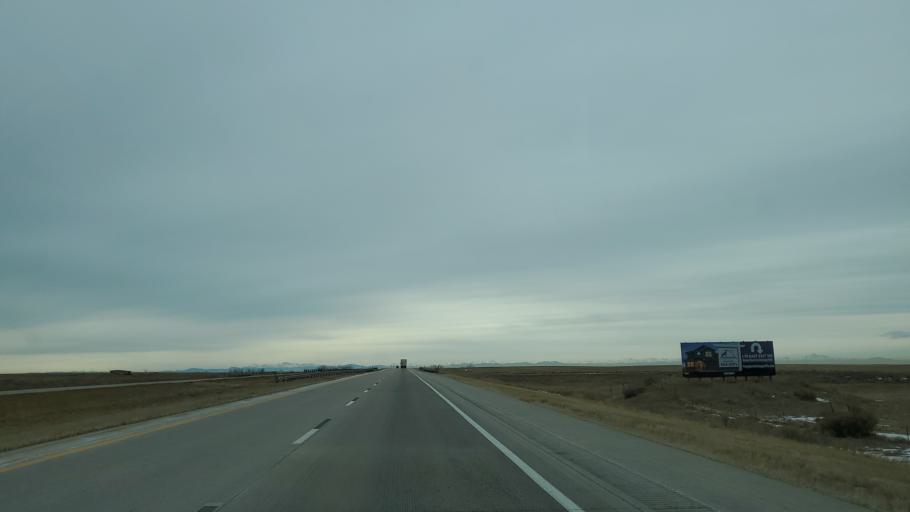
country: US
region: Colorado
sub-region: Adams County
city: Bennett
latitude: 39.7388
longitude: -104.4690
